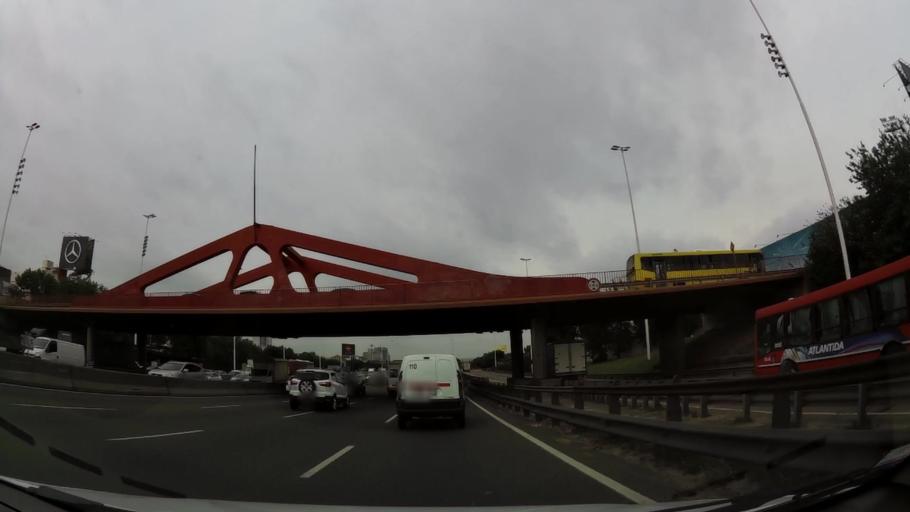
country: AR
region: Buenos Aires
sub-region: Partido de Vicente Lopez
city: Olivos
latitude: -34.5411
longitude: -58.4805
